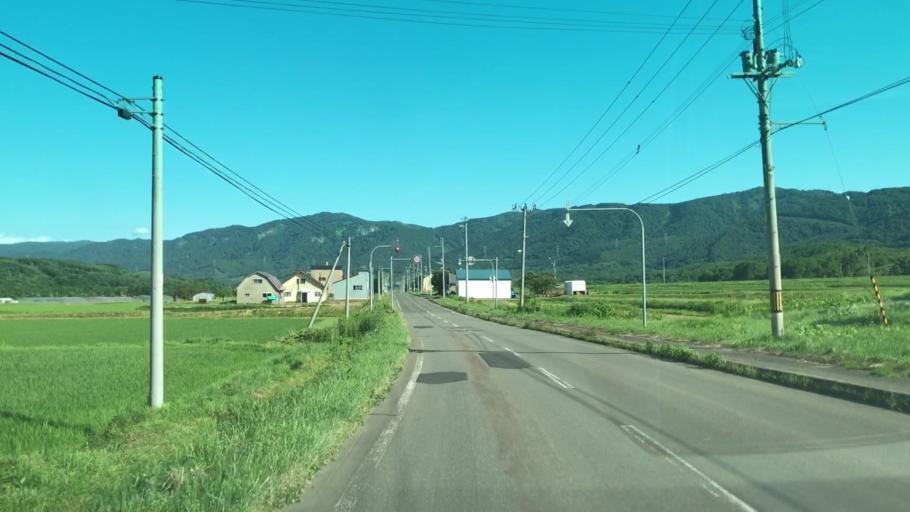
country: JP
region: Hokkaido
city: Yoichi
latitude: 43.0587
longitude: 140.7141
